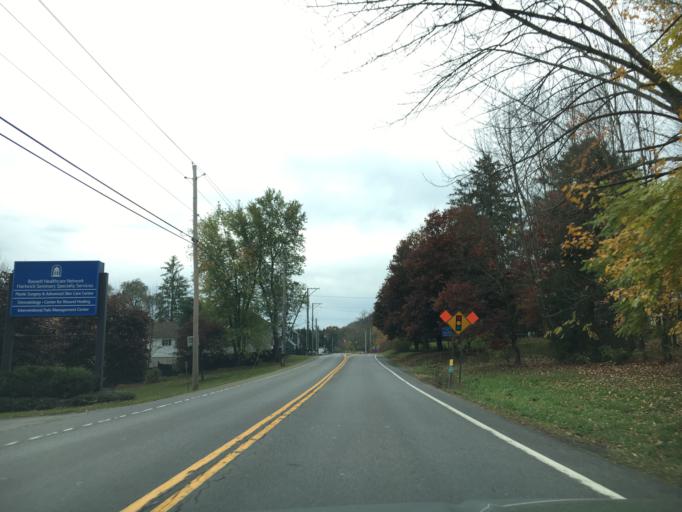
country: US
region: New York
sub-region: Otsego County
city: Cooperstown
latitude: 42.6411
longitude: -74.9653
